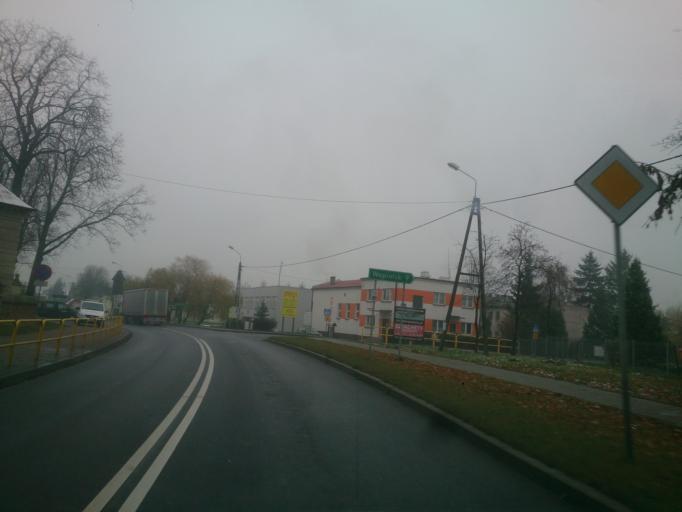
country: PL
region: Kujawsko-Pomorskie
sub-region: Powiat brodnicki
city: Brodnica
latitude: 53.1693
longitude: 19.3862
